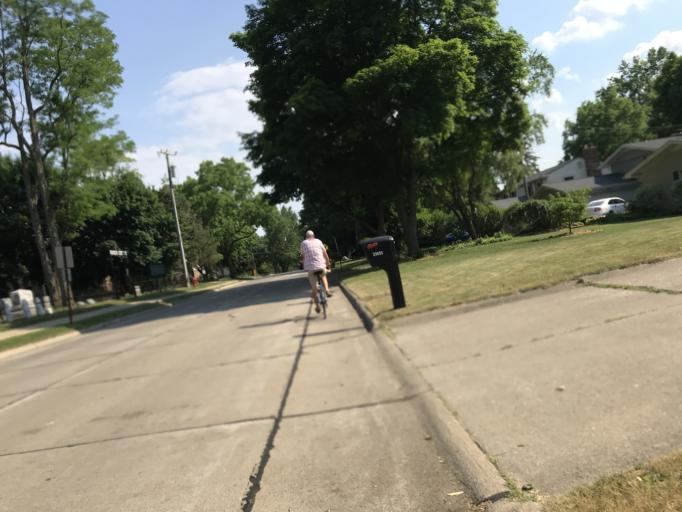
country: US
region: Michigan
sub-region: Oakland County
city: Farmington
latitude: 42.4642
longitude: -83.3863
